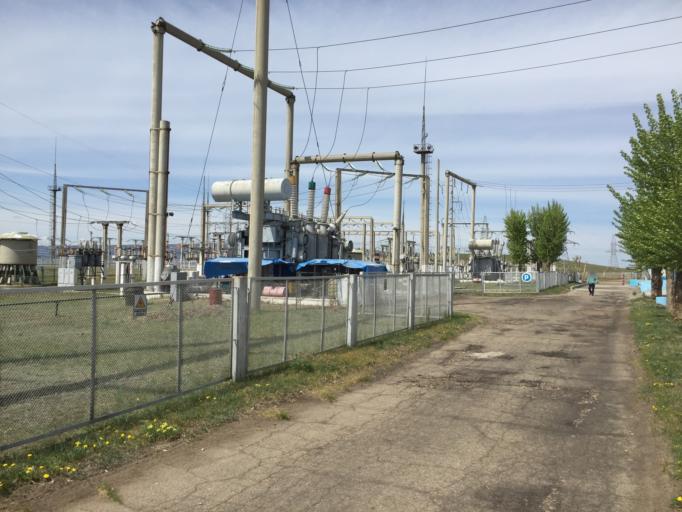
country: MN
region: Darhan Uul
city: Darhan
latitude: 49.3966
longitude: 105.9473
